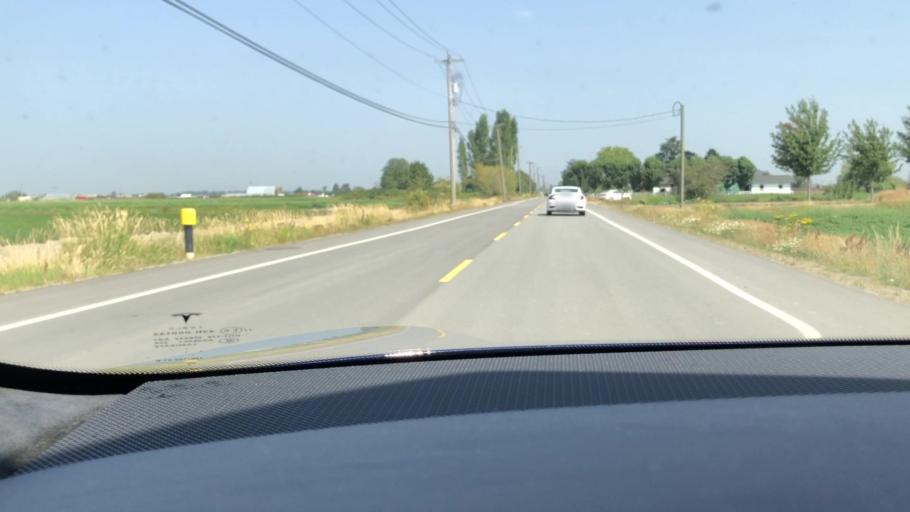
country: CA
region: British Columbia
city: Ladner
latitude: 49.0457
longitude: -123.0796
